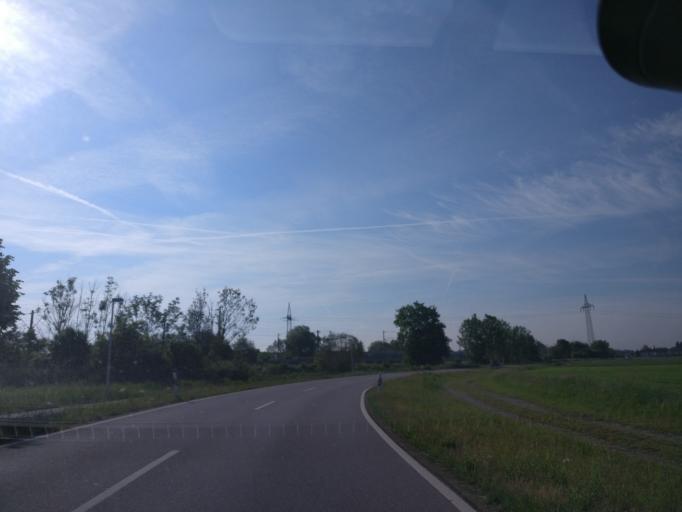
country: DE
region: Bavaria
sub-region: Upper Bavaria
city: Karlsfeld
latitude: 48.2240
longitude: 11.4538
